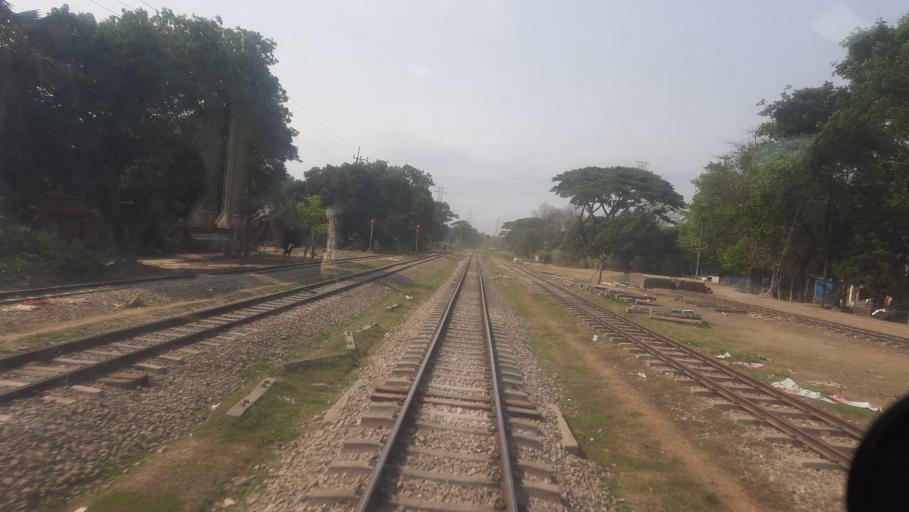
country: BD
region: Chittagong
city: Chittagong
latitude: 22.4113
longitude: 91.7555
